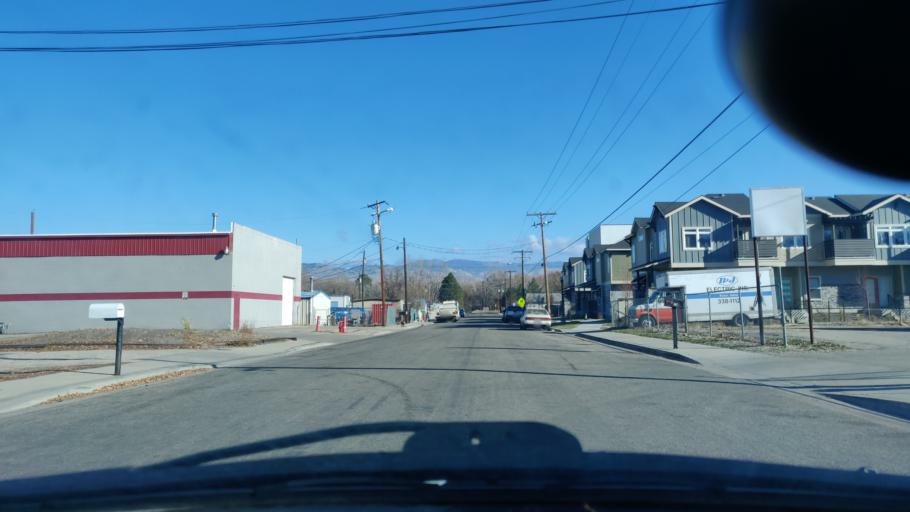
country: US
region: Idaho
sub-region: Ada County
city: Garden City
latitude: 43.6367
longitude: -116.2475
